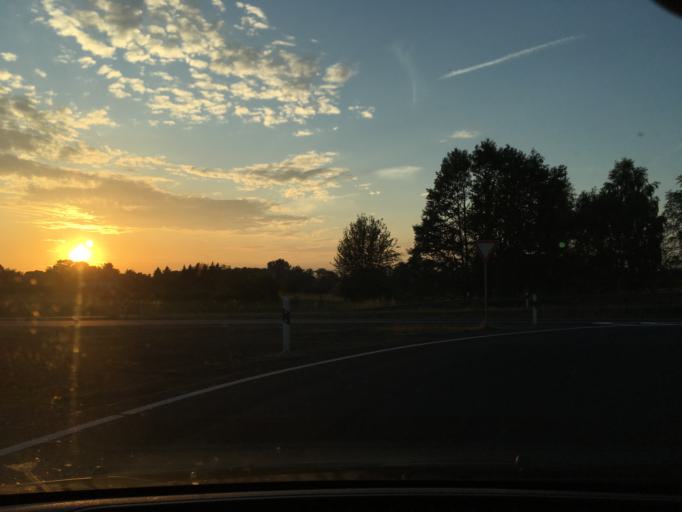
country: DE
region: Lower Saxony
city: Wrestedt
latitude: 52.9156
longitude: 10.5286
